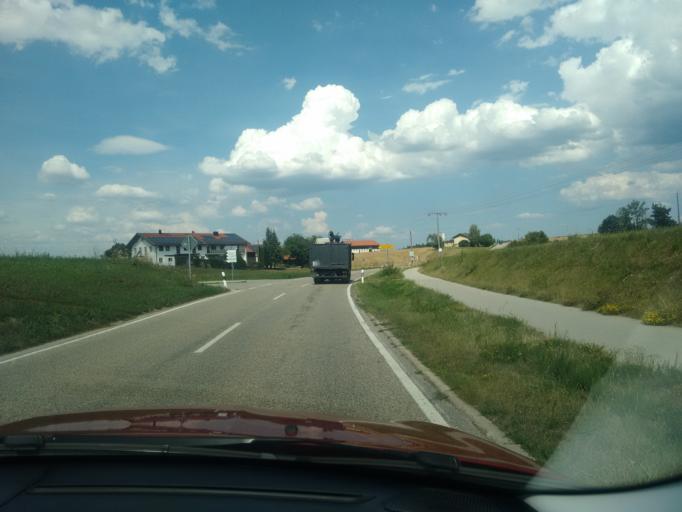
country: DE
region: Bavaria
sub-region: Upper Bavaria
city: Kirchweidach
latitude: 48.0924
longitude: 12.6530
